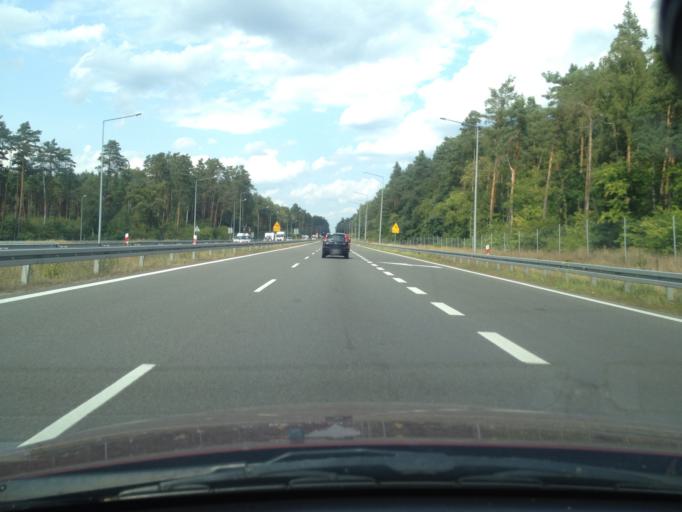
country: PL
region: West Pomeranian Voivodeship
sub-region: Powiat goleniowski
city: Goleniow
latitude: 53.6246
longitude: 14.8189
